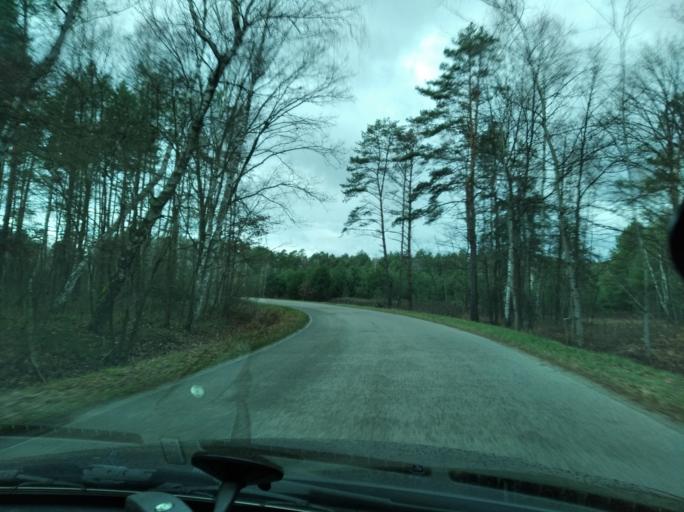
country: PL
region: Subcarpathian Voivodeship
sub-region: Powiat lancucki
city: Zolynia
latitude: 50.1392
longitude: 22.2837
